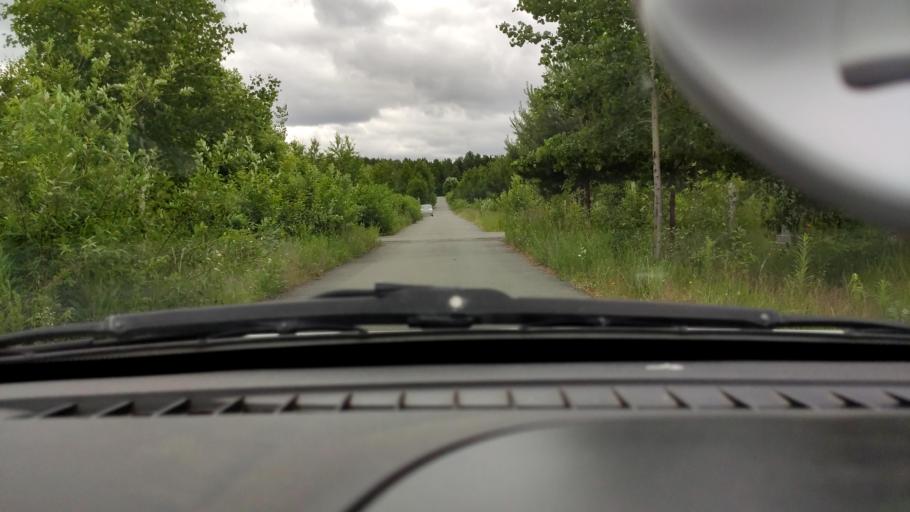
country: RU
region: Perm
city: Kondratovo
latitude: 58.0647
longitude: 56.1599
